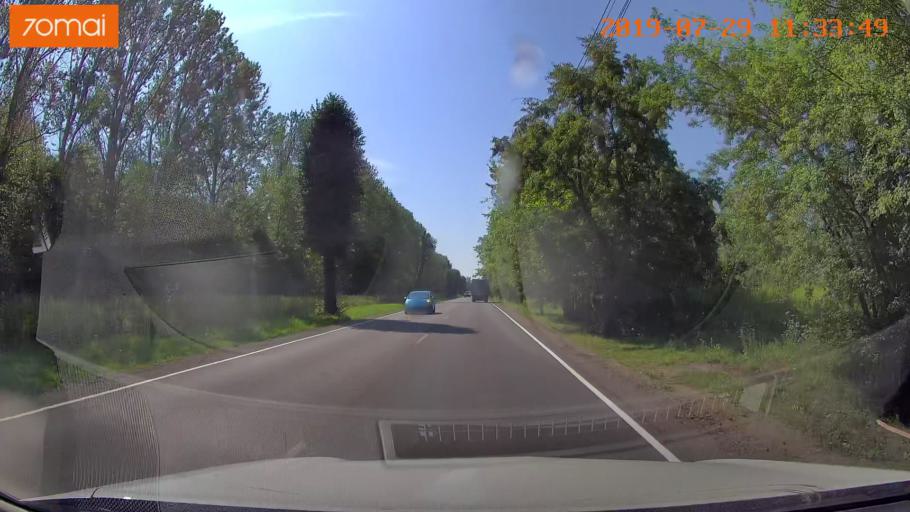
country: RU
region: Kaliningrad
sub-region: Gorod Kaliningrad
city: Kaliningrad
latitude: 54.6613
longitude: 20.5409
